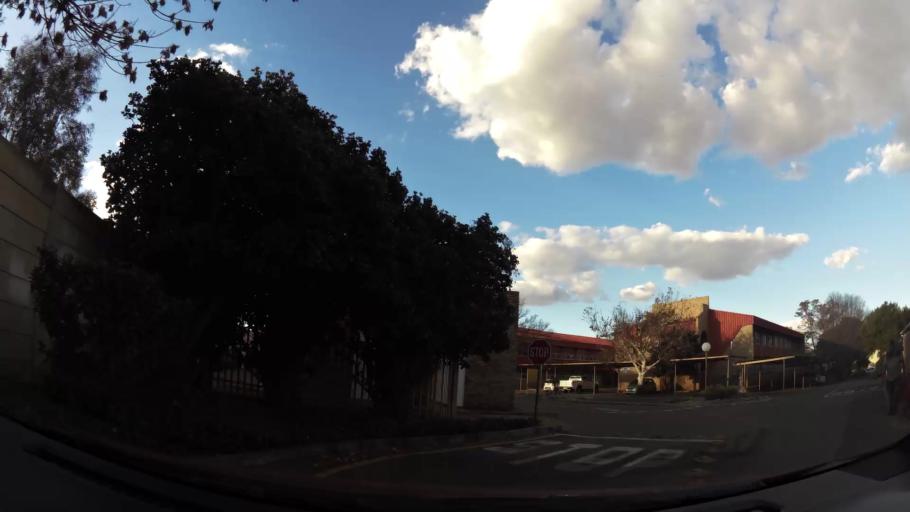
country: ZA
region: North-West
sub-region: Dr Kenneth Kaunda District Municipality
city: Potchefstroom
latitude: -26.6849
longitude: 27.0919
